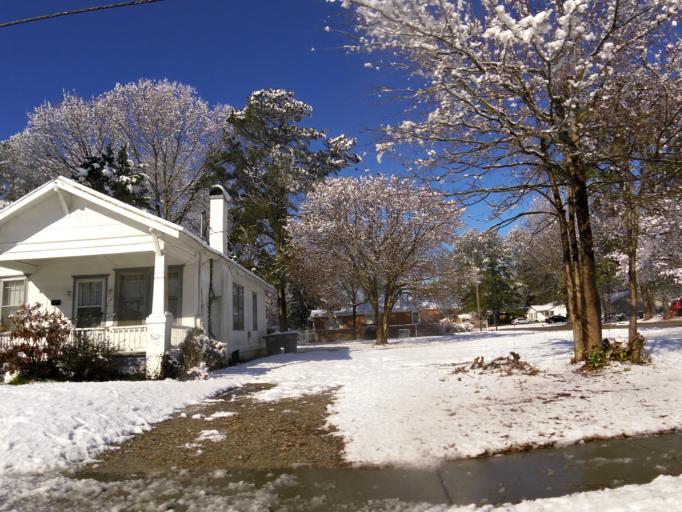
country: US
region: North Carolina
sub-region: Nash County
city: Rocky Mount
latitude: 35.9123
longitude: -77.8097
